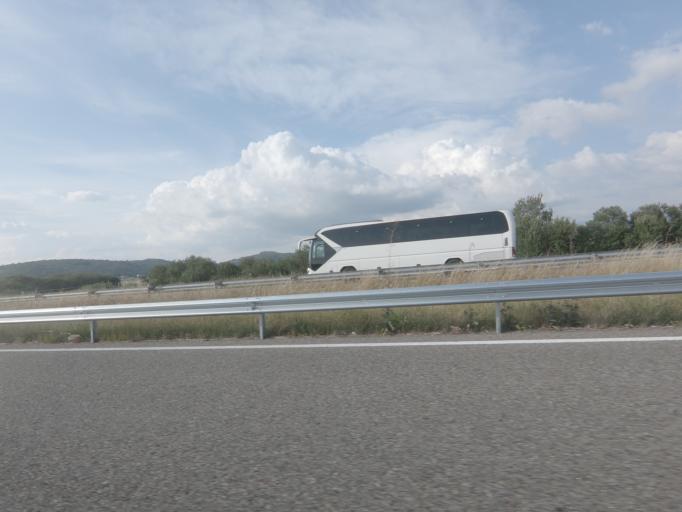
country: ES
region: Galicia
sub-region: Provincia de Ourense
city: Xinzo de Limia
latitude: 42.0589
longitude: -7.6746
